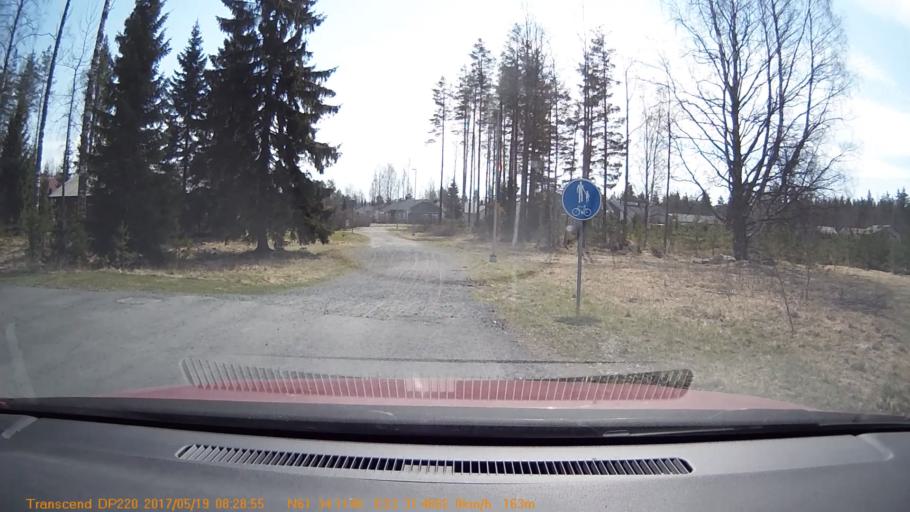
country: FI
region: Pirkanmaa
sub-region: Tampere
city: Yloejaervi
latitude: 61.5686
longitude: 23.5244
